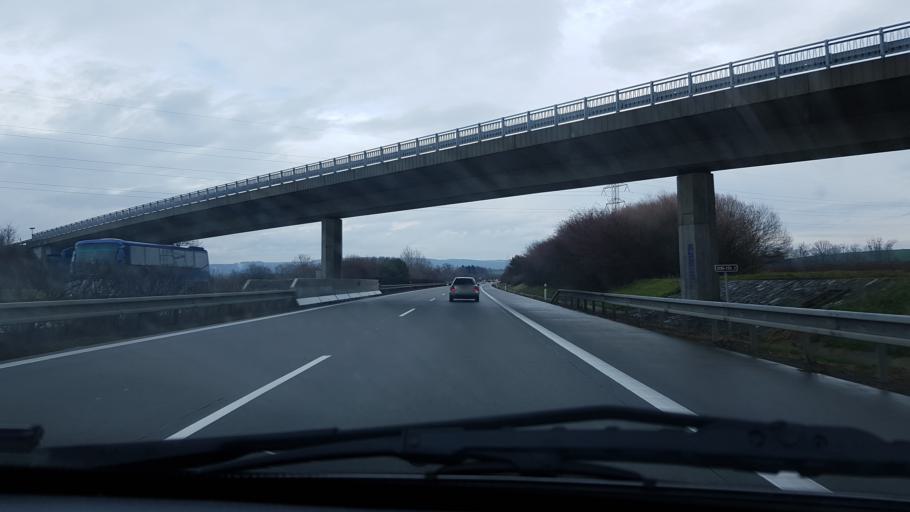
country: CZ
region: Olomoucky
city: Velky Tynec
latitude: 49.5686
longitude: 17.3396
